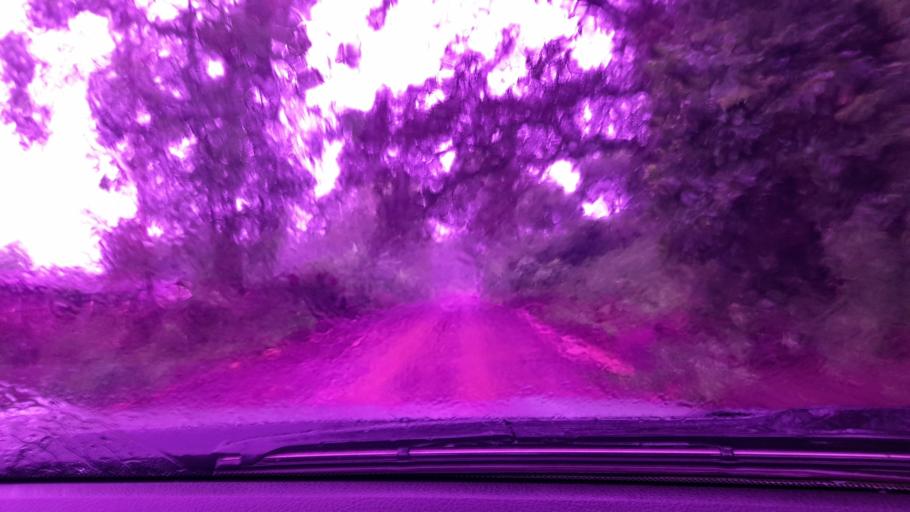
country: ET
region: Oromiya
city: Metu
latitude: 8.3485
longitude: 35.5990
